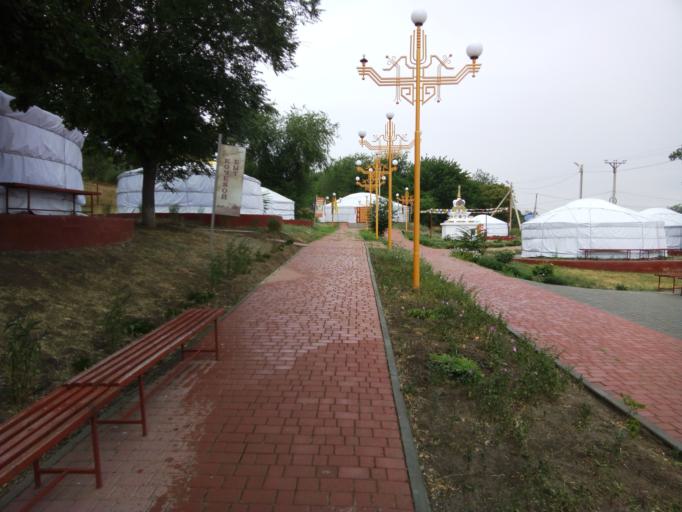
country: RU
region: Kalmykiya
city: Elista
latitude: 46.3064
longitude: 44.2475
